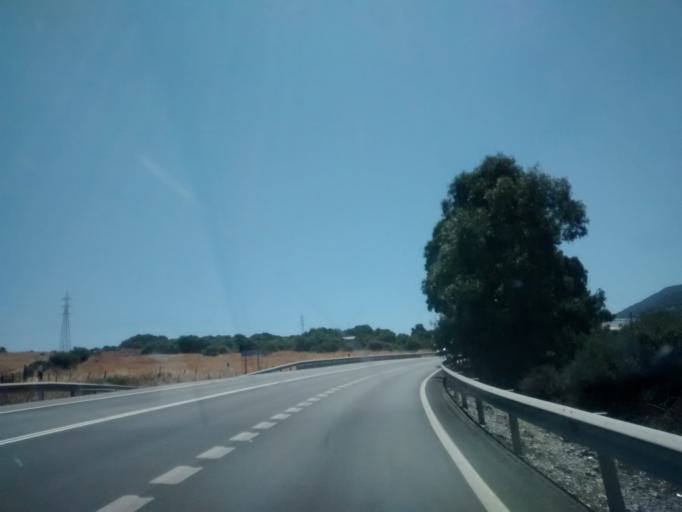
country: ES
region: Andalusia
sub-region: Provincia de Cadiz
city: Algeciras
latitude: 36.1006
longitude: -5.4651
